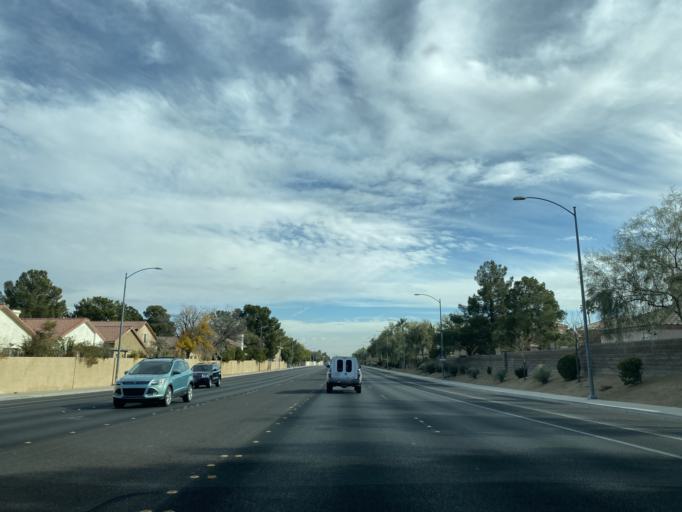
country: US
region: Nevada
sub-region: Clark County
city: Las Vegas
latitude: 36.2464
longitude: -115.2159
